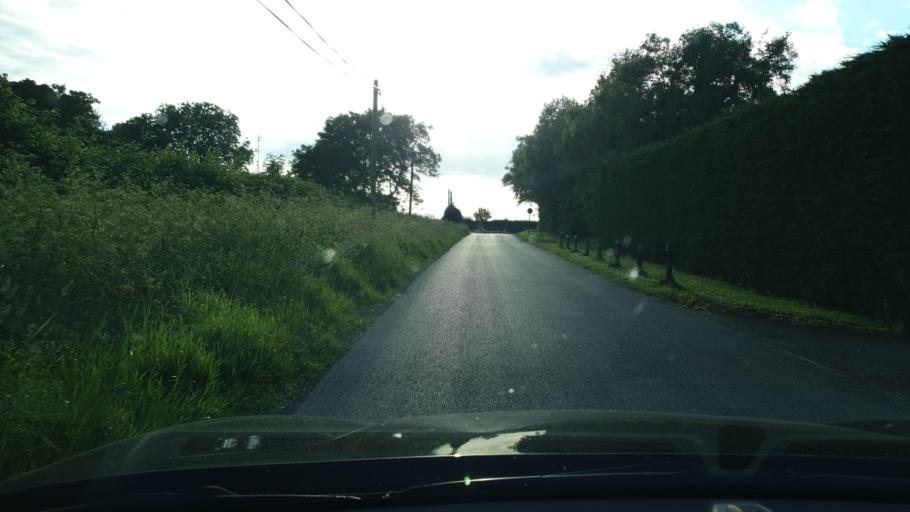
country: IE
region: Leinster
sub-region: Fingal County
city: Blanchardstown
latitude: 53.4384
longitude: -6.3944
